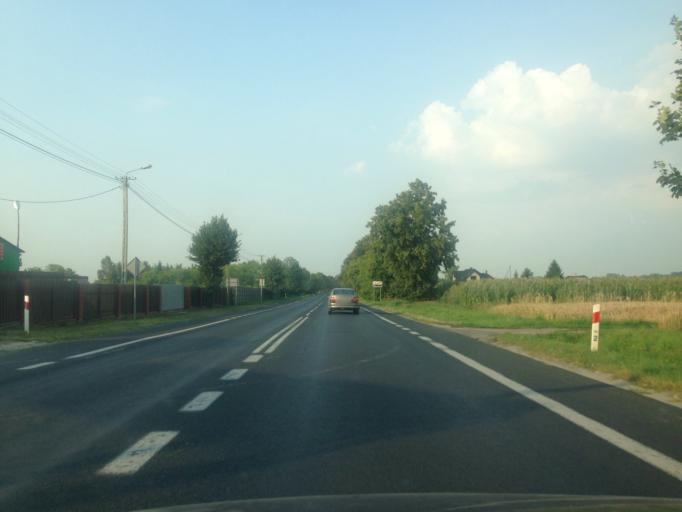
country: PL
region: Kujawsko-Pomorskie
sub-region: Powiat lipnowski
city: Lipno
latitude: 52.8144
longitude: 19.1430
